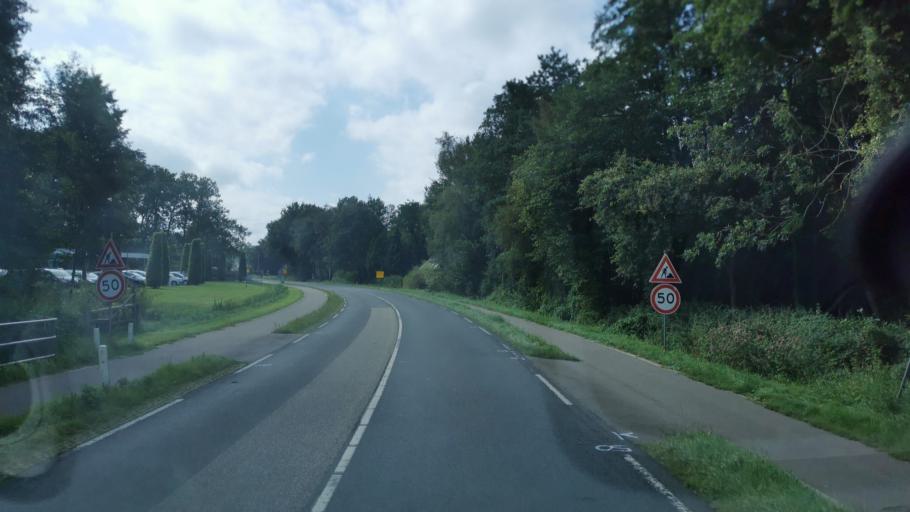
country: NL
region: Overijssel
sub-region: Gemeente Hengelo
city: Hengelo
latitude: 52.3021
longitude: 6.8318
